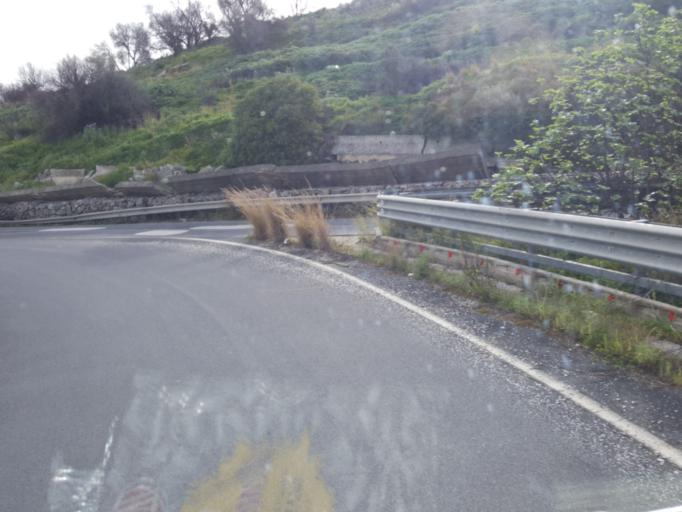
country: IT
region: Sicily
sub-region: Provincia di Siracusa
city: Melilli
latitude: 37.2160
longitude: 15.1543
